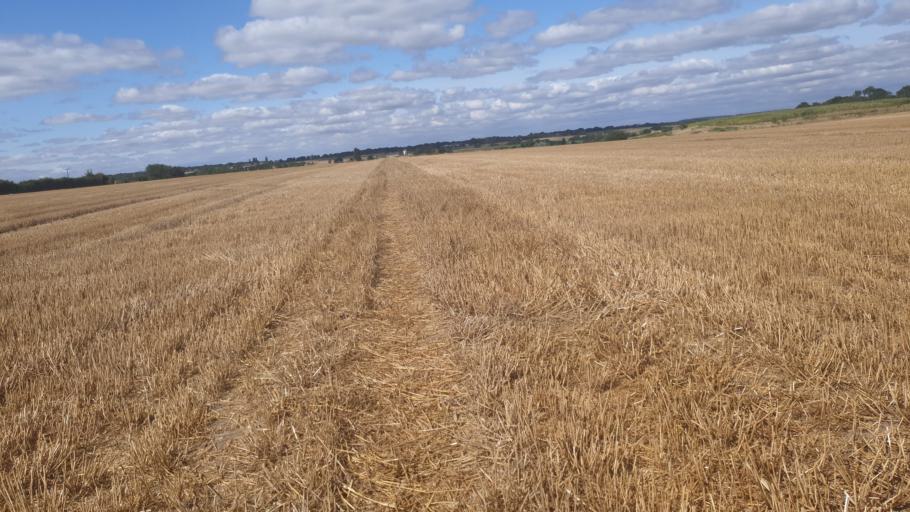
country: GB
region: England
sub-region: Essex
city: Dovercourt
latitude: 51.9187
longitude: 1.2212
